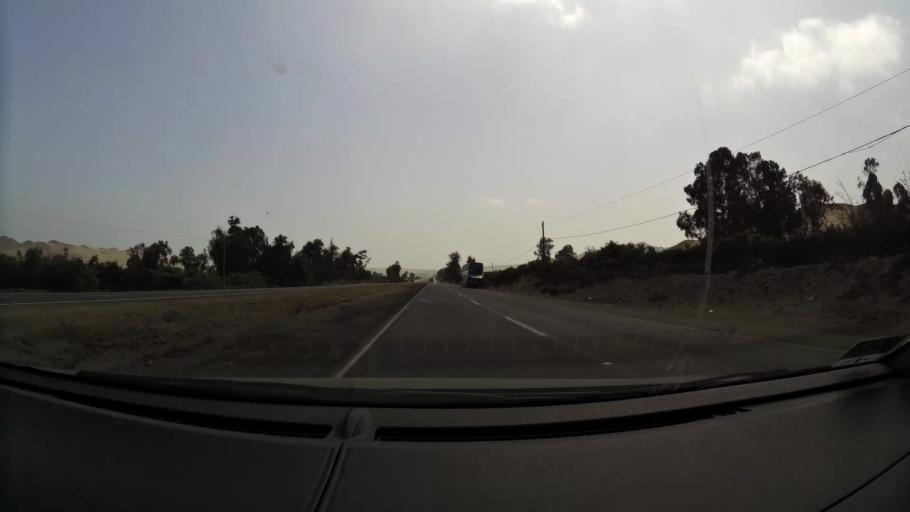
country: PE
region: Lima
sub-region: Provincia de Huaral
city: Huaral
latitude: -11.4595
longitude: -77.3169
